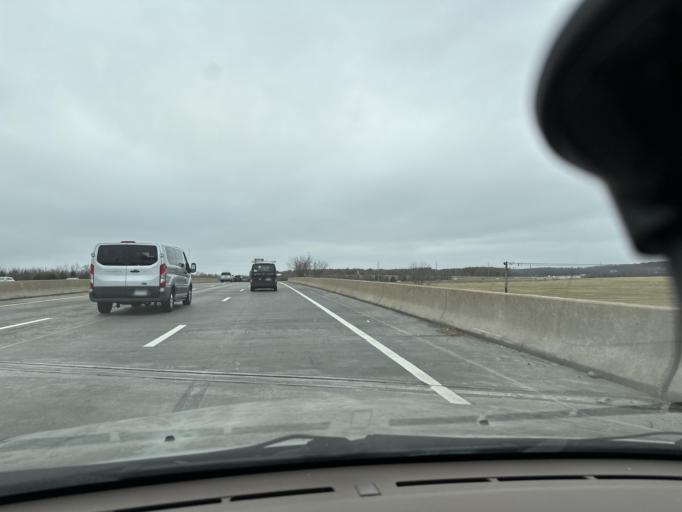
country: US
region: Arkansas
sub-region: Washington County
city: Johnson
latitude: 36.1119
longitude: -94.1629
